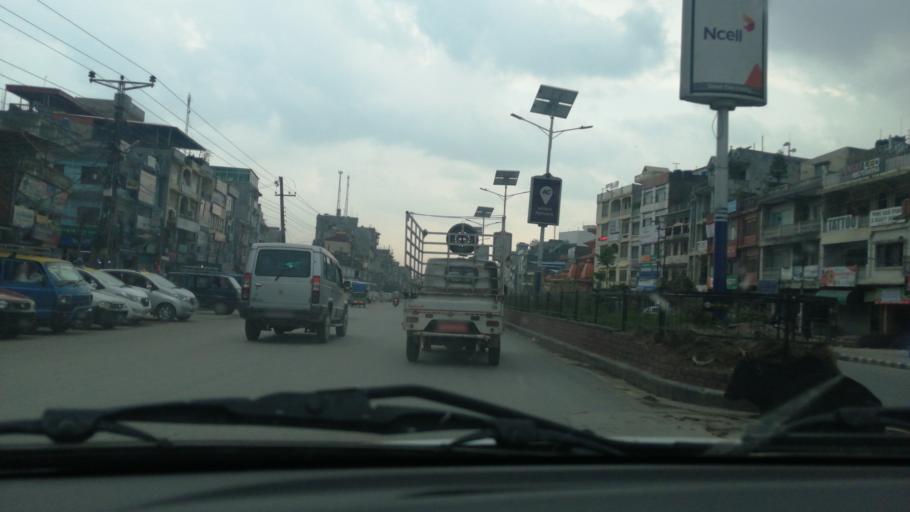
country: NP
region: Western Region
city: Butwal
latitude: 27.7017
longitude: 83.4663
